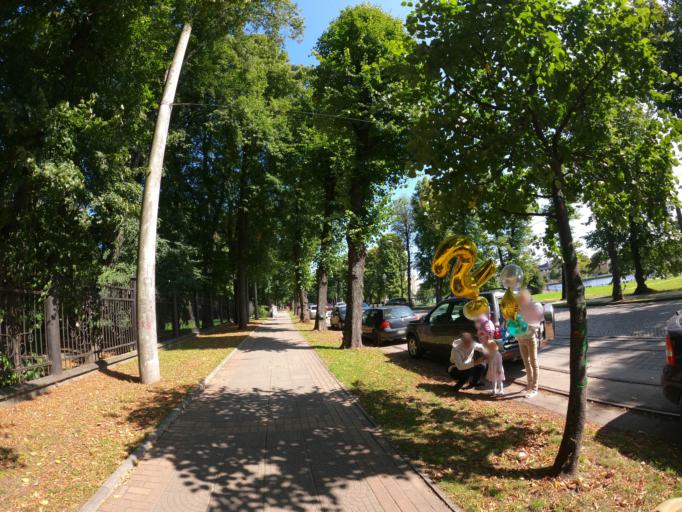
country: RU
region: Kaliningrad
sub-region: Gorod Kaliningrad
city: Kaliningrad
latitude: 54.7271
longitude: 20.5154
